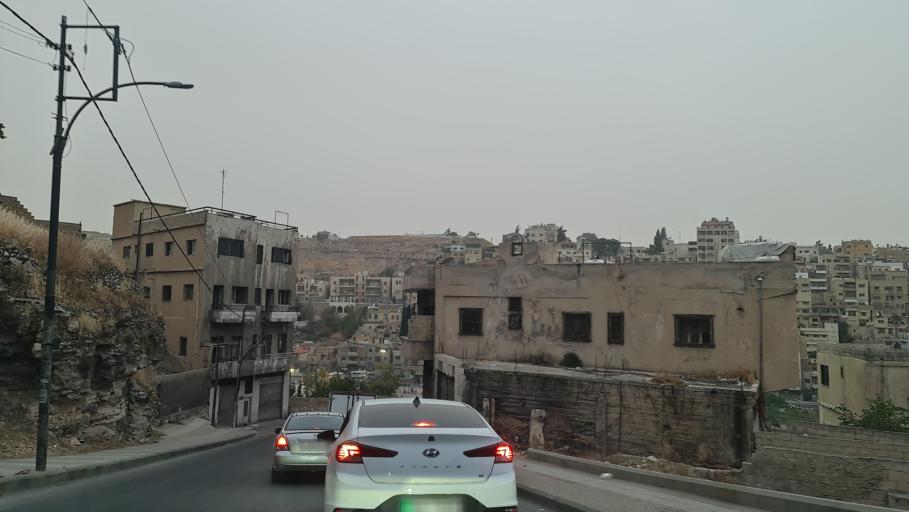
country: JO
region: Amman
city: Amman
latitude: 31.9511
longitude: 35.9403
